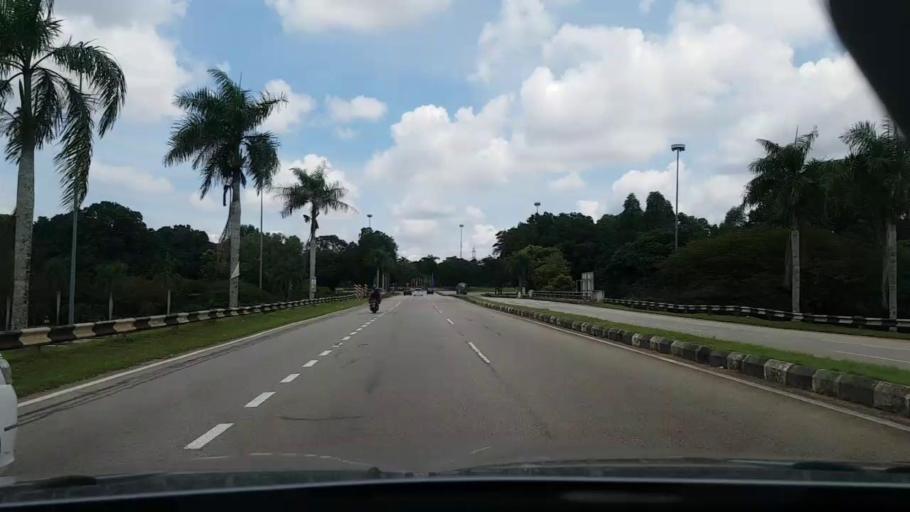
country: MY
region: Pahang
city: Kuantan
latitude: 3.8347
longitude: 103.2909
